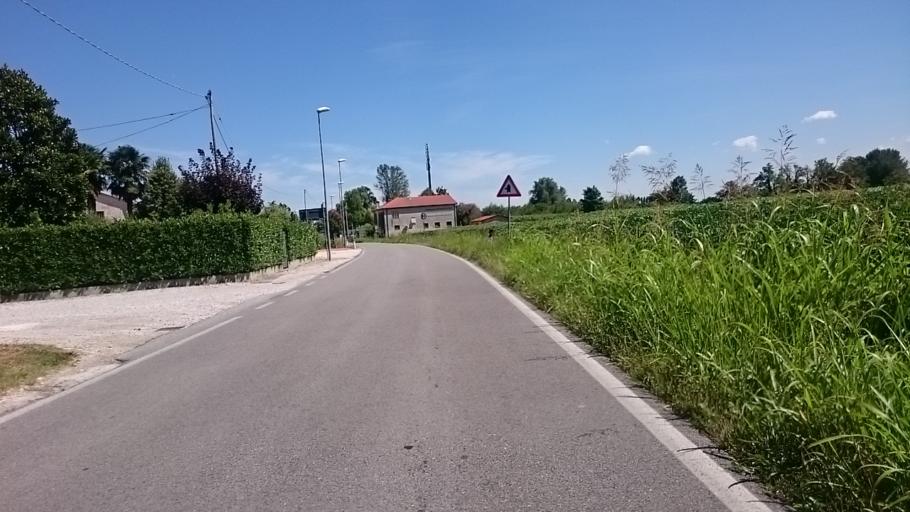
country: IT
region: Veneto
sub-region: Provincia di Venezia
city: Fiesso d'Artico
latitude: 45.4415
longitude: 12.0227
